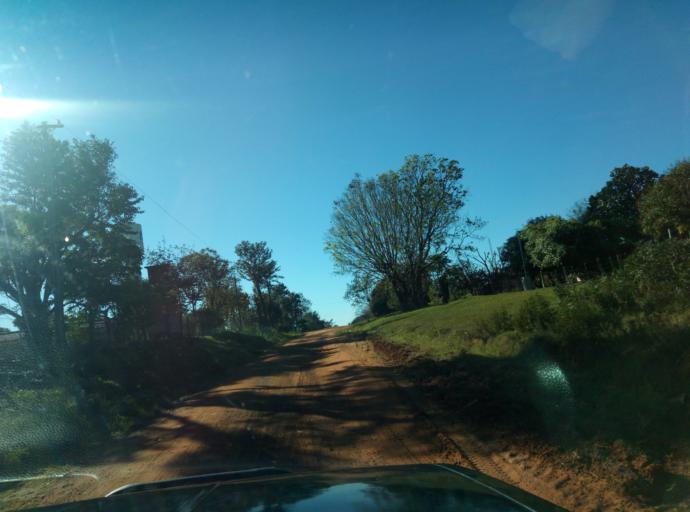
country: PY
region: Caaguazu
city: Carayao
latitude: -25.1584
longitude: -56.2928
